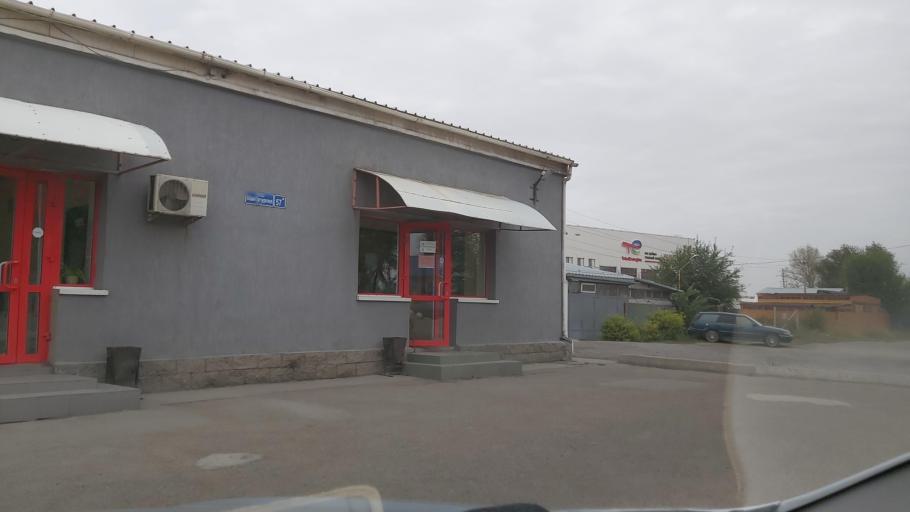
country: KZ
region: Almaty Oblysy
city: Energeticheskiy
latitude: 43.4368
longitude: 77.0287
